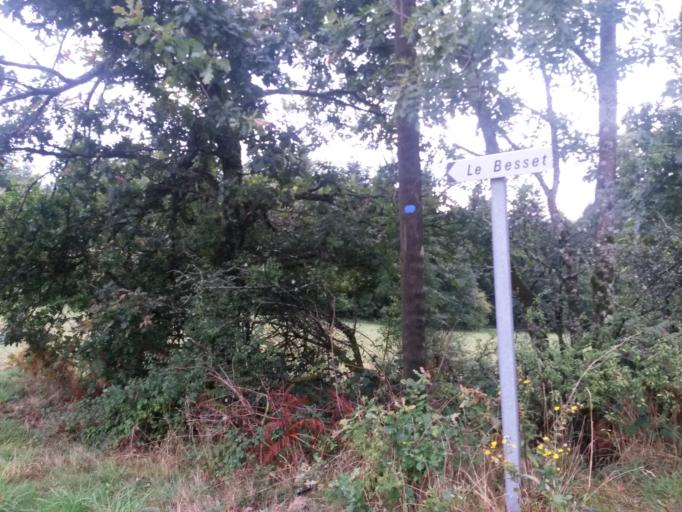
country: FR
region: Auvergne
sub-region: Departement du Puy-de-Dome
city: Thiers
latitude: 45.8713
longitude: 3.5591
